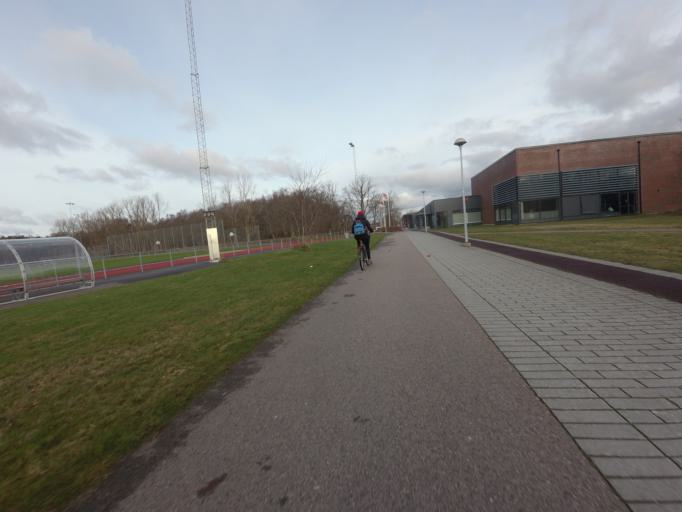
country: SE
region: Skane
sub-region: Hoganas Kommun
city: Hoganas
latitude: 56.1846
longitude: 12.5661
